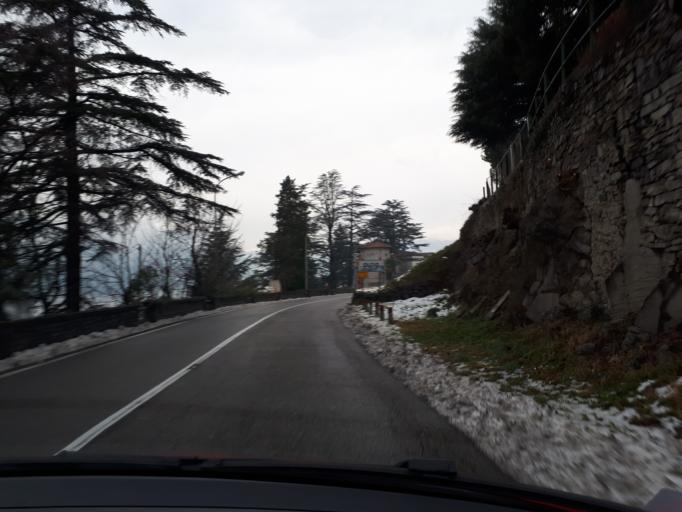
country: IT
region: Lombardy
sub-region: Provincia di Lecco
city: Mandello del Lario
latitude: 45.9302
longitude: 9.3124
